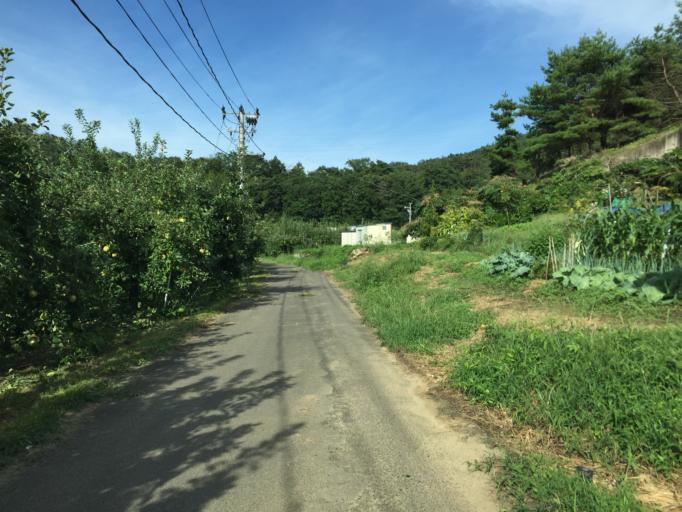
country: JP
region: Fukushima
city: Hobaramachi
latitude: 37.7978
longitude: 140.5144
